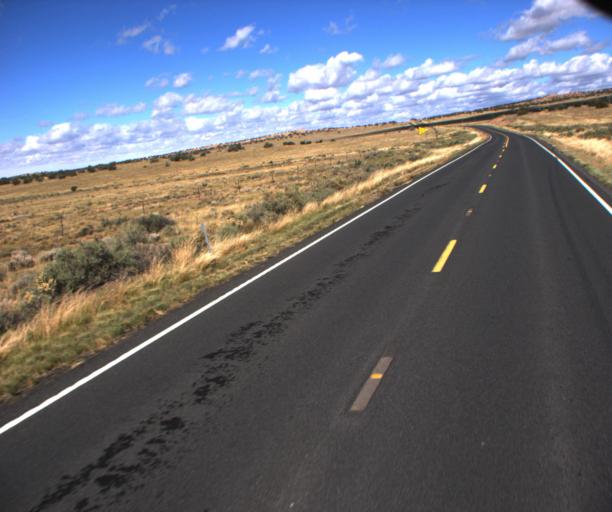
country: US
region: Arizona
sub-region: Apache County
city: Houck
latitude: 35.0565
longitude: -109.2771
